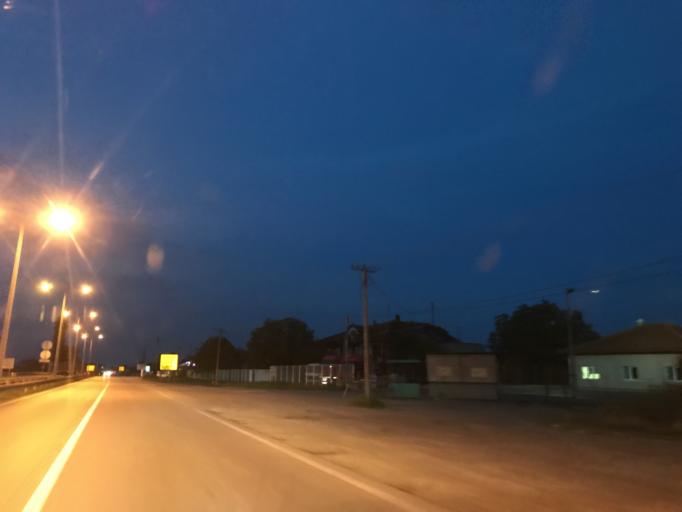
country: RS
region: Central Serbia
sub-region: Podunavski Okrug
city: Smederevo
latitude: 44.5804
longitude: 20.9834
